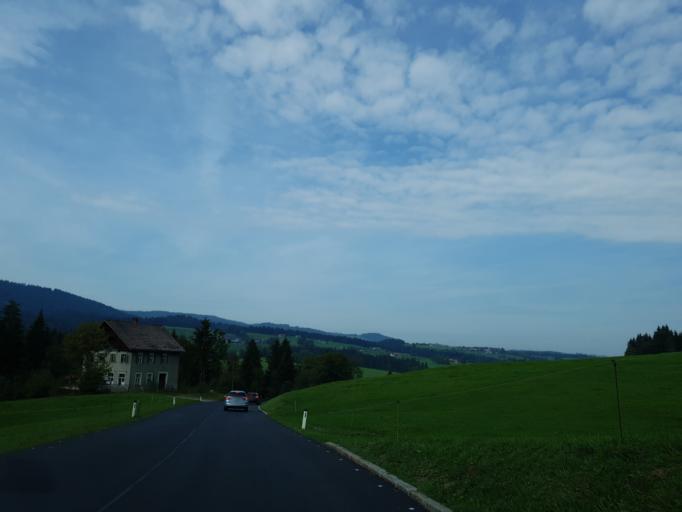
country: AT
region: Vorarlberg
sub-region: Politischer Bezirk Bregenz
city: Doren
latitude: 47.5110
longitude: 9.8672
